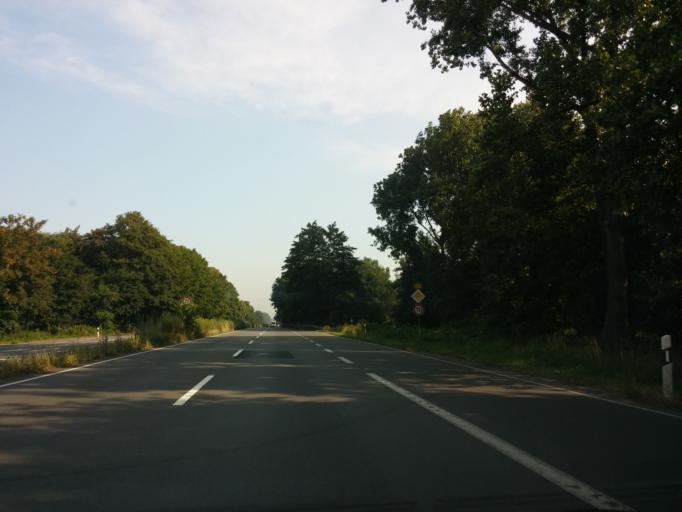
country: DE
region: North Rhine-Westphalia
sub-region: Regierungsbezirk Munster
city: Gladbeck
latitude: 51.5370
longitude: 6.9848
